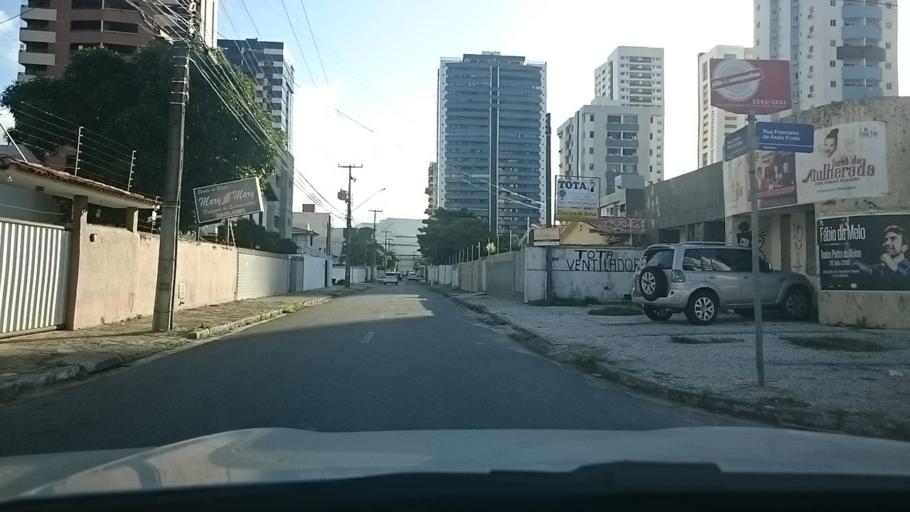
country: BR
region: Paraiba
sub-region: Joao Pessoa
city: Joao Pessoa
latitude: -7.0991
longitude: -34.8405
